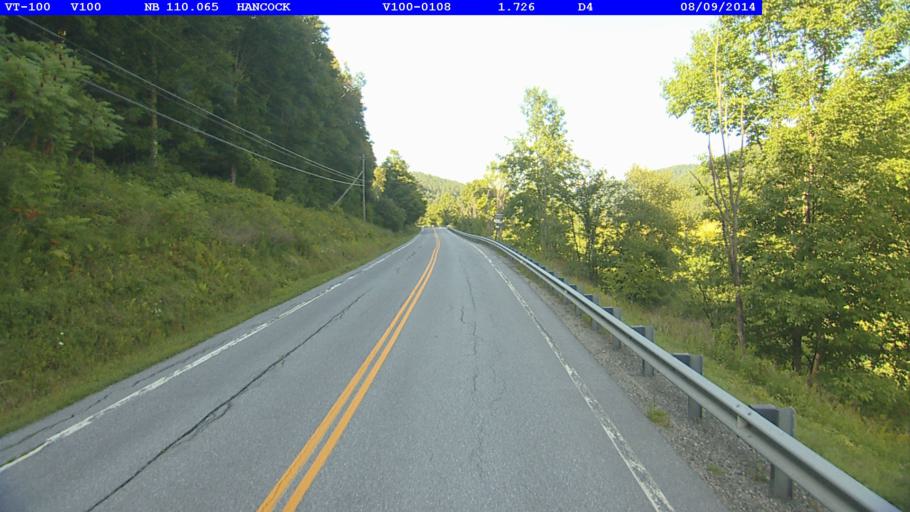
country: US
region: Vermont
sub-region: Orange County
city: Randolph
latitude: 43.9337
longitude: -72.8420
